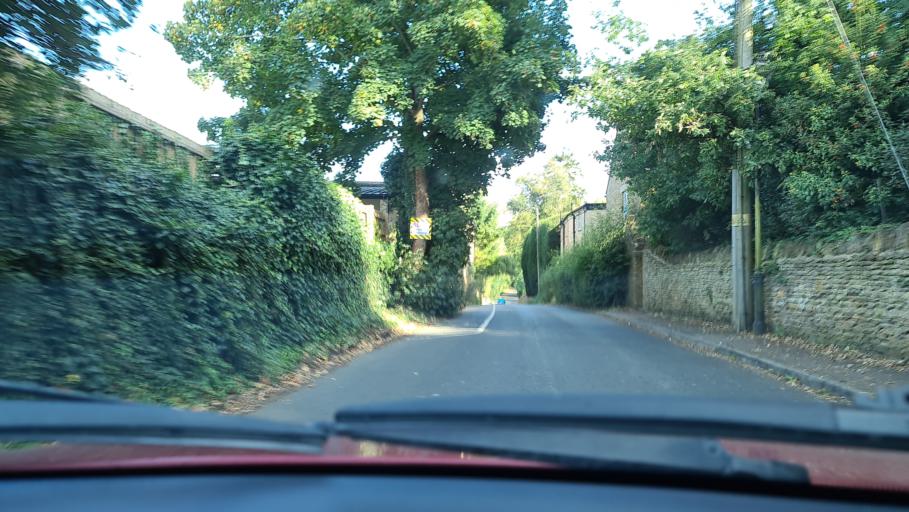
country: GB
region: England
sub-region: Oxfordshire
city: Adderbury
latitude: 52.0226
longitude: -1.2664
